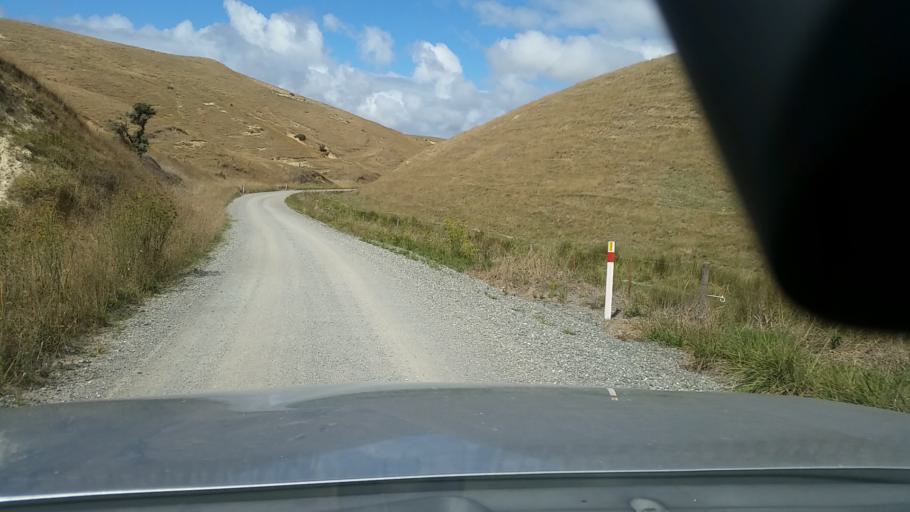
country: NZ
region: Marlborough
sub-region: Marlborough District
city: Blenheim
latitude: -41.6973
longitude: 174.1474
